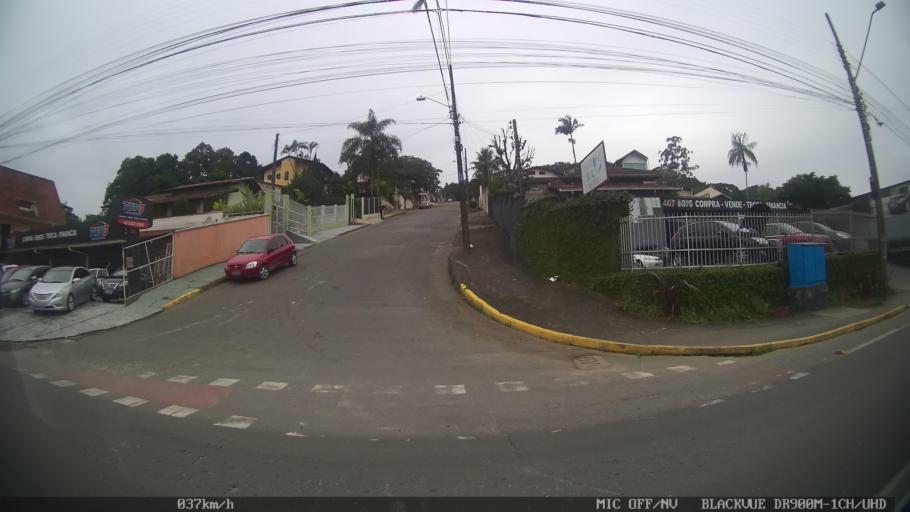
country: BR
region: Santa Catarina
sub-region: Joinville
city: Joinville
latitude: -26.2772
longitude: -48.8325
